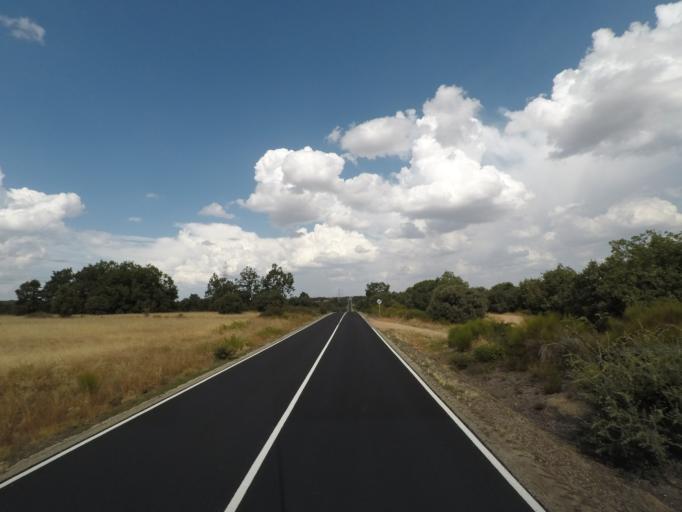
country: ES
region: Castille and Leon
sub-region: Provincia de Zamora
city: Fermoselle
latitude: 41.3068
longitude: -6.3157
